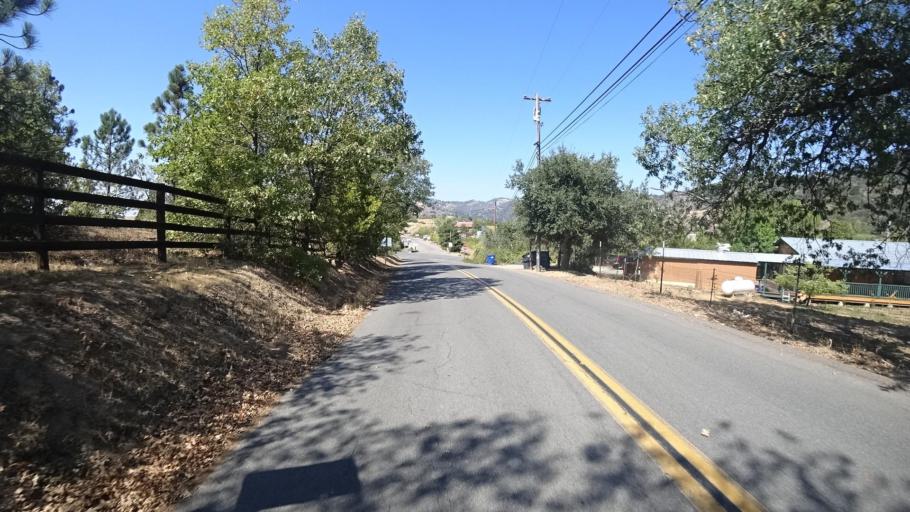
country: US
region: California
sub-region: San Diego County
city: Julian
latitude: 33.1027
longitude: -116.6037
